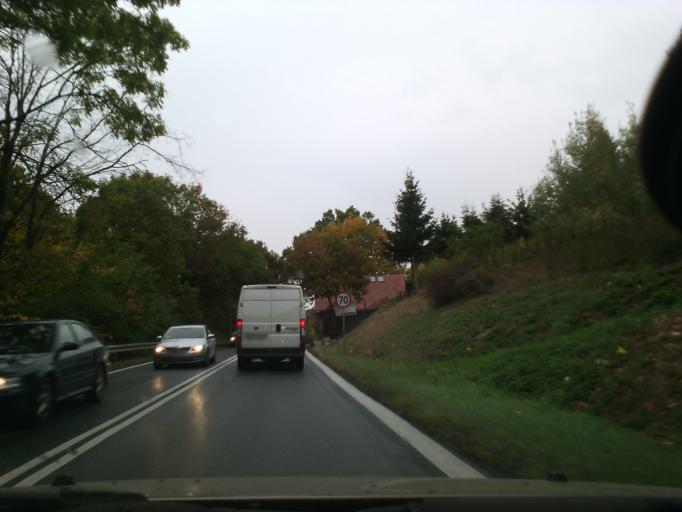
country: PL
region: Lower Silesian Voivodeship
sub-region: Powiat jaworski
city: Bolkow
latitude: 50.9246
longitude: 16.0776
